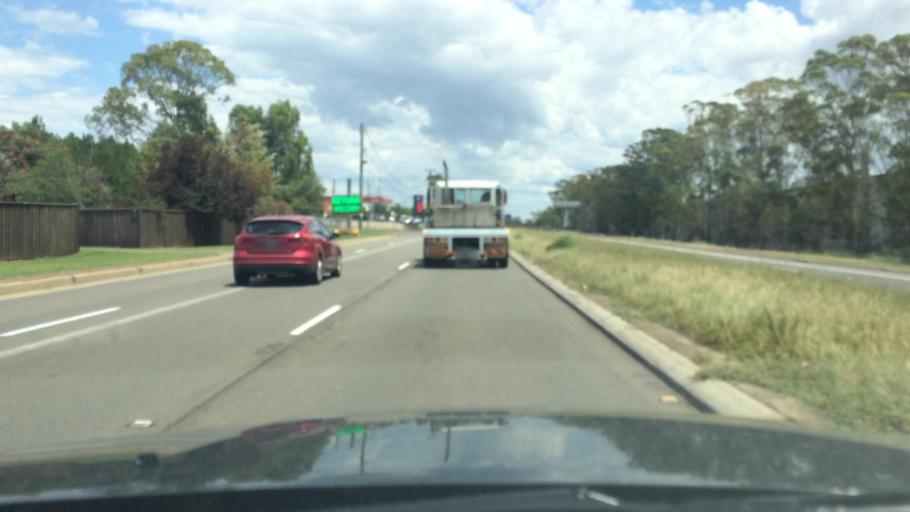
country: AU
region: New South Wales
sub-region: Campbelltown Municipality
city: Glenfield
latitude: -33.9618
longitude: 150.8824
